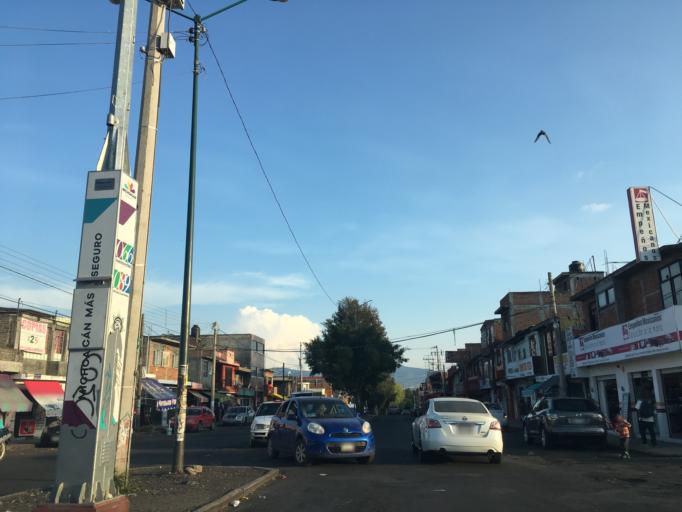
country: MX
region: Michoacan
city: Morelia
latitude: 19.7173
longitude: -101.2162
